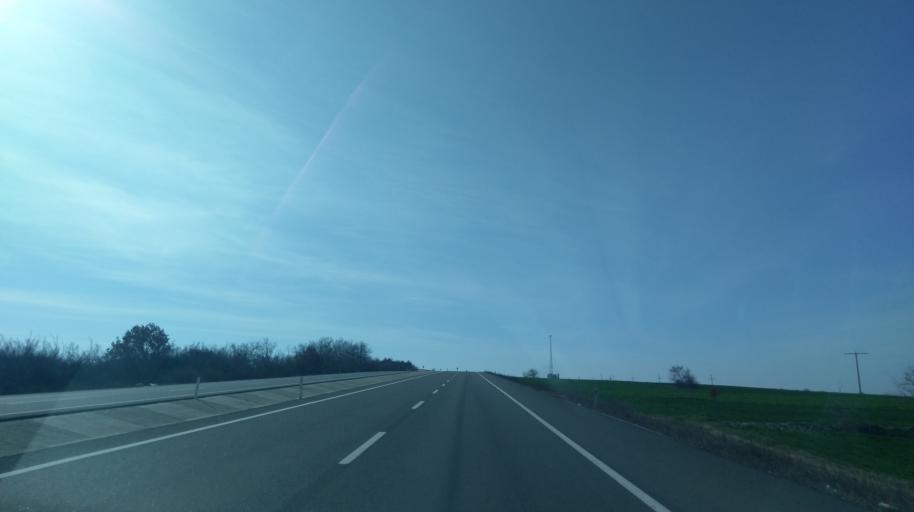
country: TR
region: Edirne
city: Hamidiye
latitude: 41.0844
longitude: 26.6396
